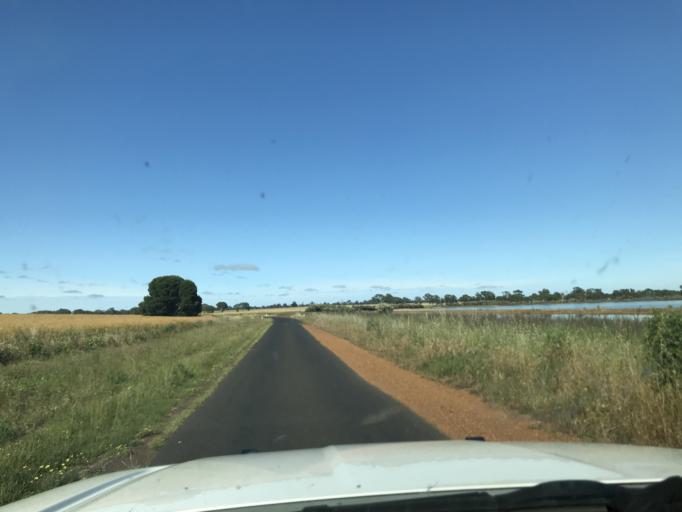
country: AU
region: Victoria
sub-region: Horsham
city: Horsham
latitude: -37.0780
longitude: 141.7497
